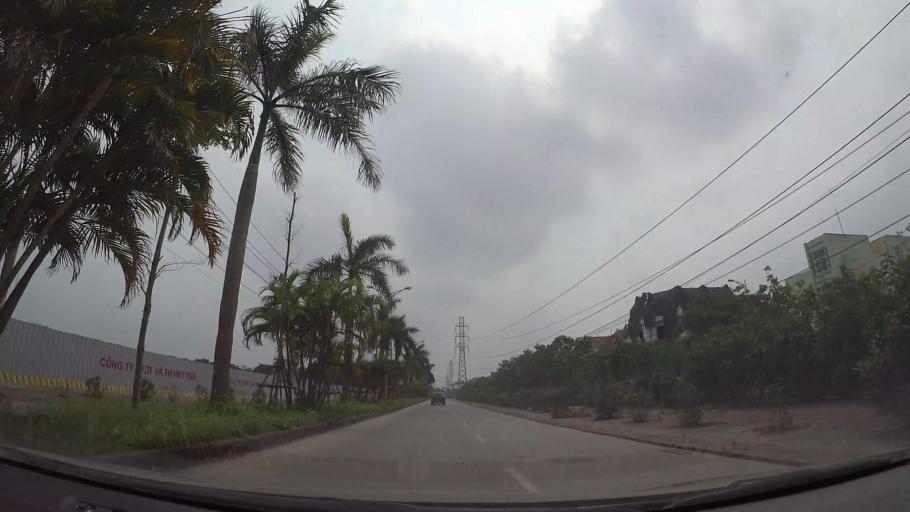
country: VN
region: Ha Noi
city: Trau Quy
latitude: 21.0655
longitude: 105.9055
